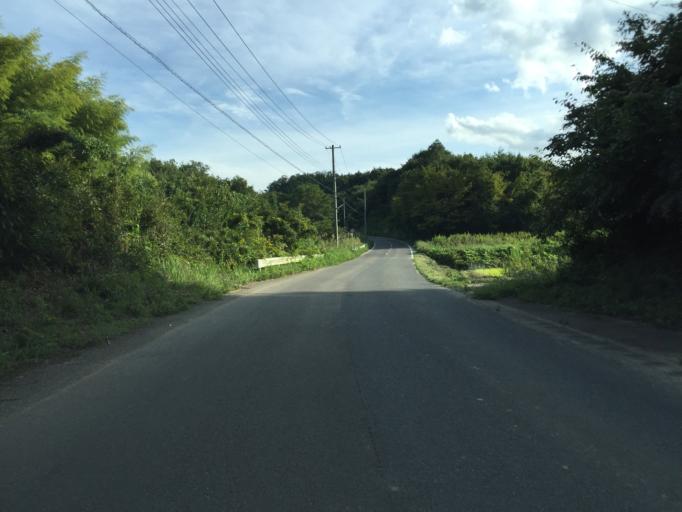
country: JP
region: Fukushima
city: Hobaramachi
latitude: 37.8020
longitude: 140.5904
